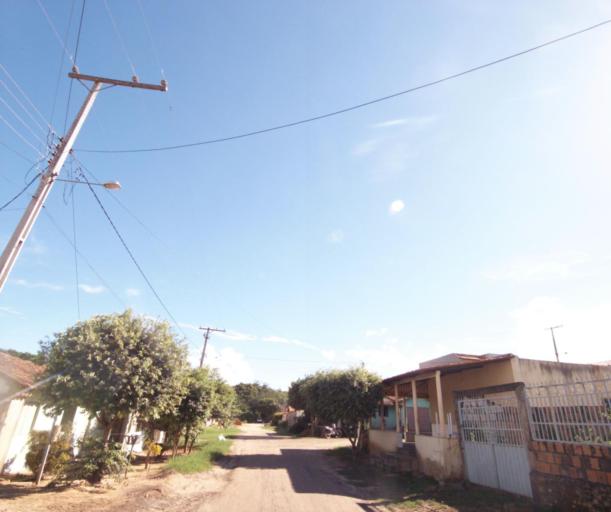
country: BR
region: Bahia
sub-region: Correntina
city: Correntina
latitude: -13.3495
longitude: -44.6356
